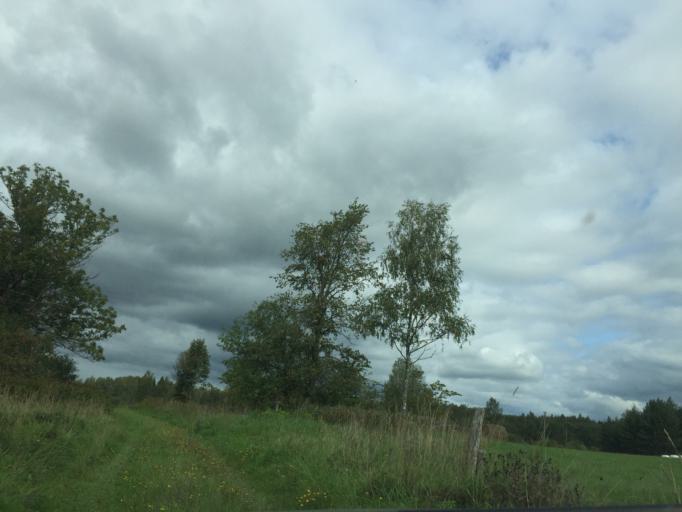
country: LV
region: Pargaujas
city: Stalbe
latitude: 57.4960
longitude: 24.9135
